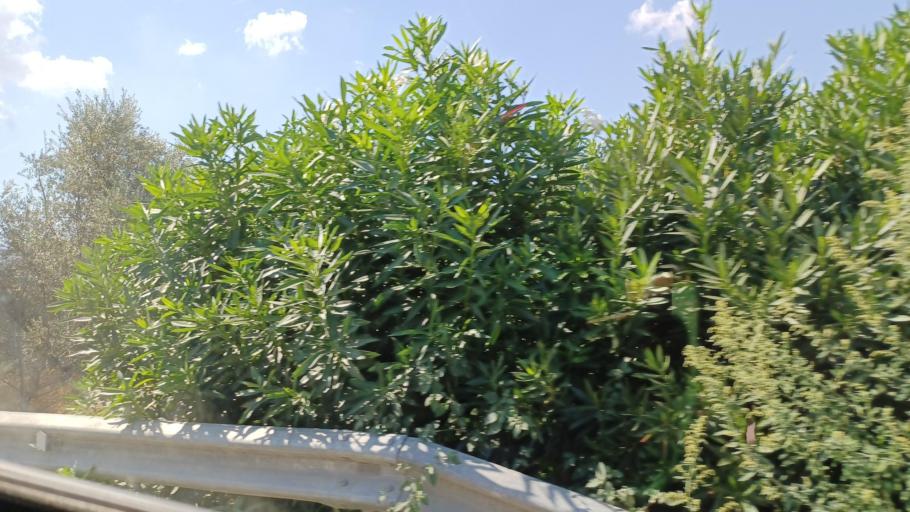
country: CY
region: Pafos
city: Polis
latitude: 34.9969
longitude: 32.4447
